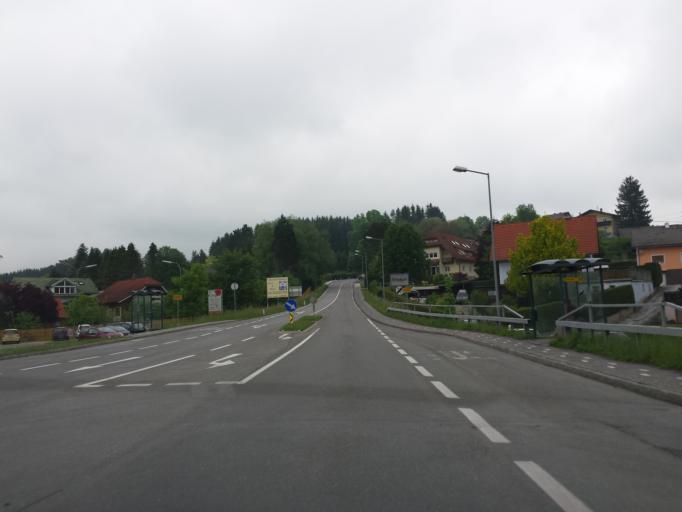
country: AT
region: Styria
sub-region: Politischer Bezirk Graz-Umgebung
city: Kumberg
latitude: 47.1501
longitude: 15.5483
